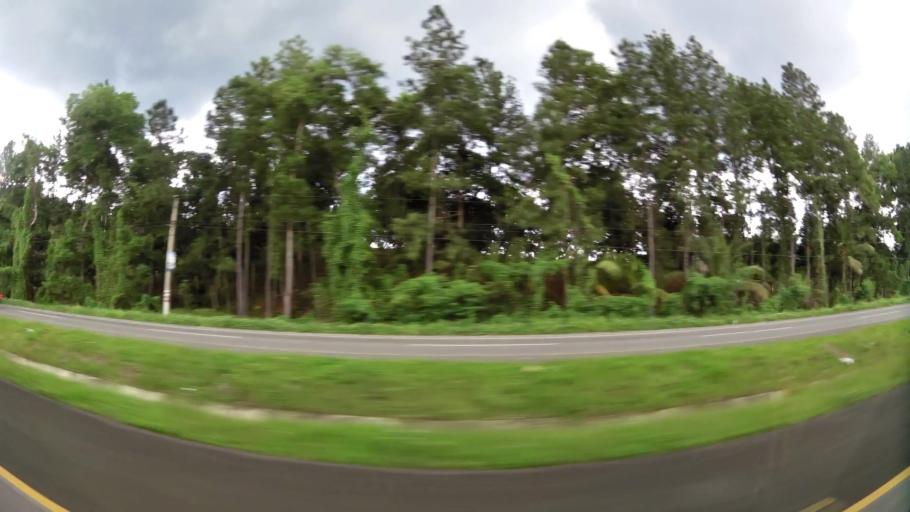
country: DO
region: San Cristobal
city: Villa Altagracia
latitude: 18.7409
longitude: -70.2310
